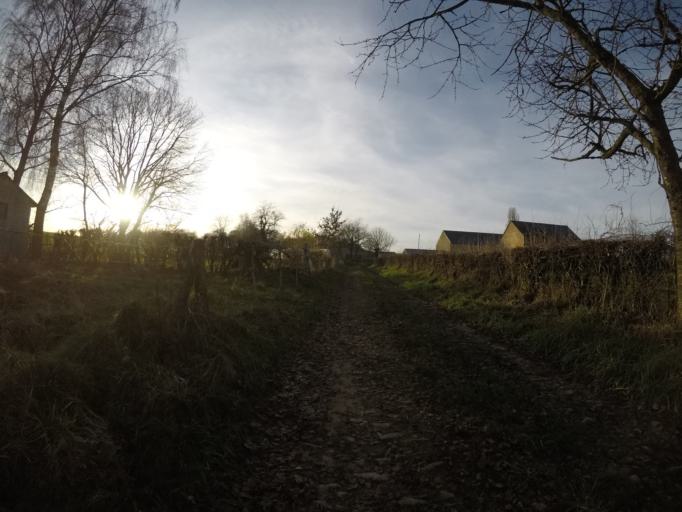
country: BE
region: Wallonia
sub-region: Province du Luxembourg
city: Tintigny
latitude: 49.6807
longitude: 5.4846
